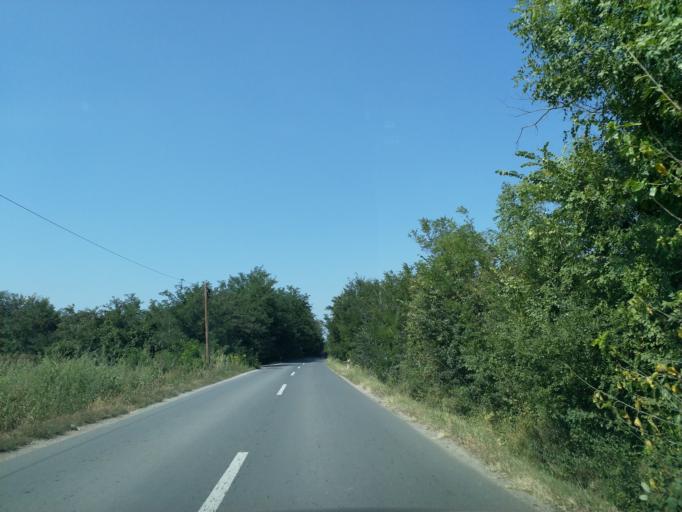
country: RS
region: Central Serbia
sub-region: Rasinski Okrug
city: Trstenik
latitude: 43.6251
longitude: 21.1592
